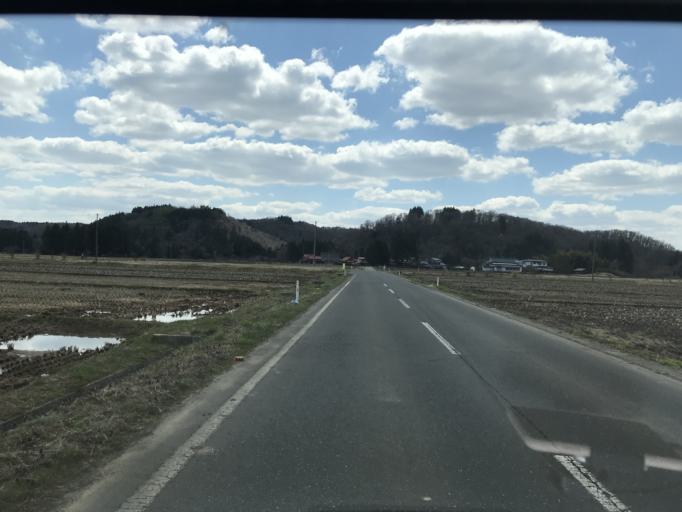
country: JP
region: Iwate
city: Ichinoseki
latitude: 38.9248
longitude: 141.0821
